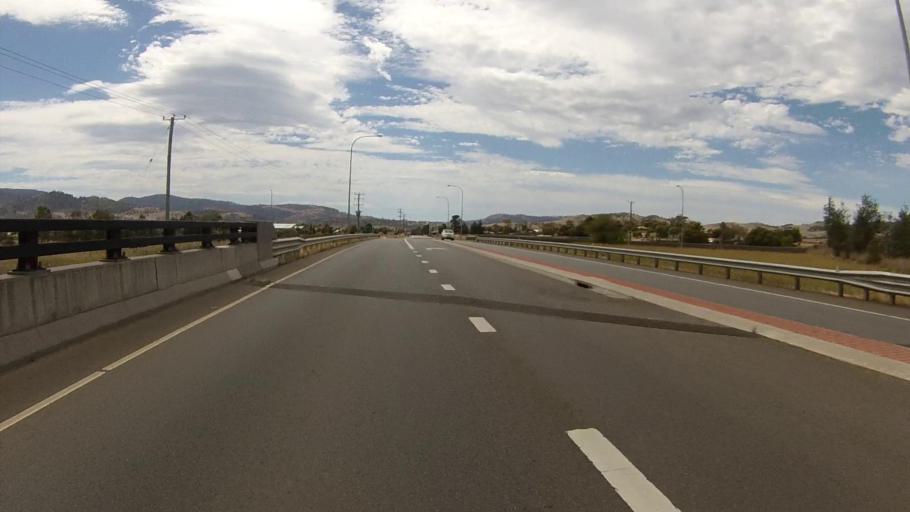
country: AU
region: Tasmania
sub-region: Brighton
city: Bridgewater
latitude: -42.6963
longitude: 147.2771
